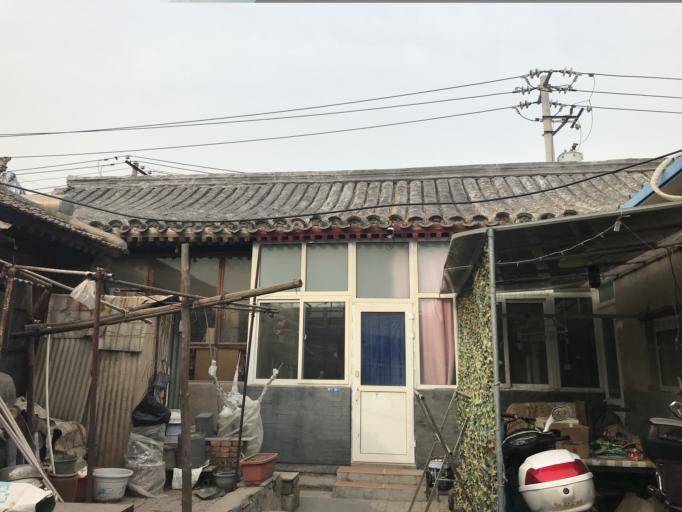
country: CN
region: Beijing
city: Beijing
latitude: 39.8898
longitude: 116.3871
